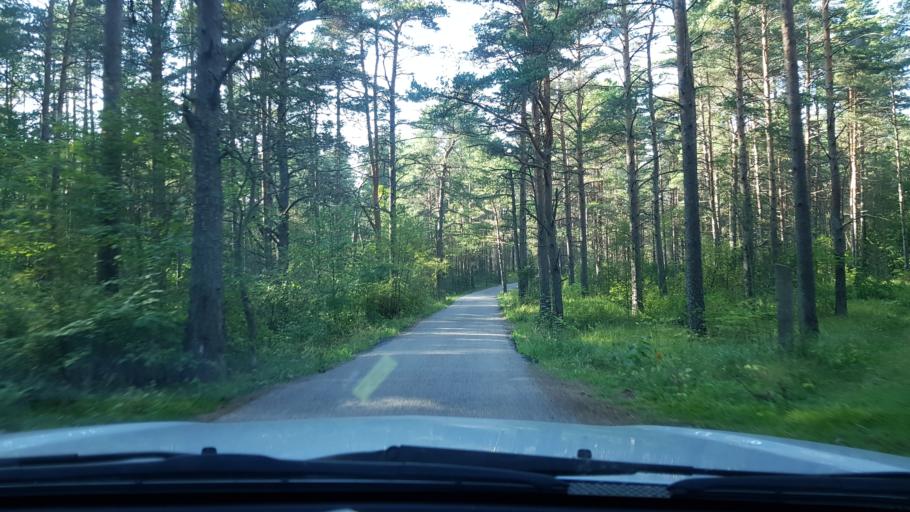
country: EE
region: Ida-Virumaa
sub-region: Narva-Joesuu linn
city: Narva-Joesuu
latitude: 59.4471
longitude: 28.0707
